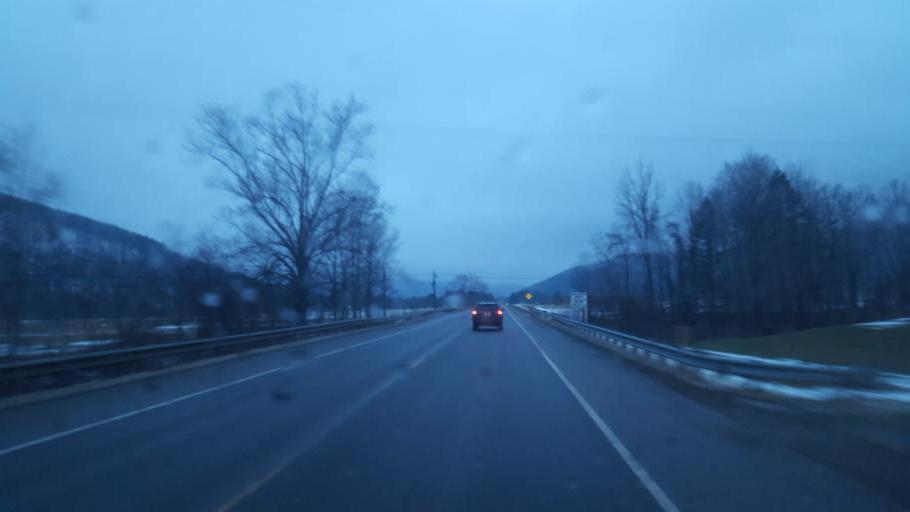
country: US
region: Pennsylvania
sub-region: McKean County
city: Port Allegany
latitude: 41.7917
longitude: -78.2429
